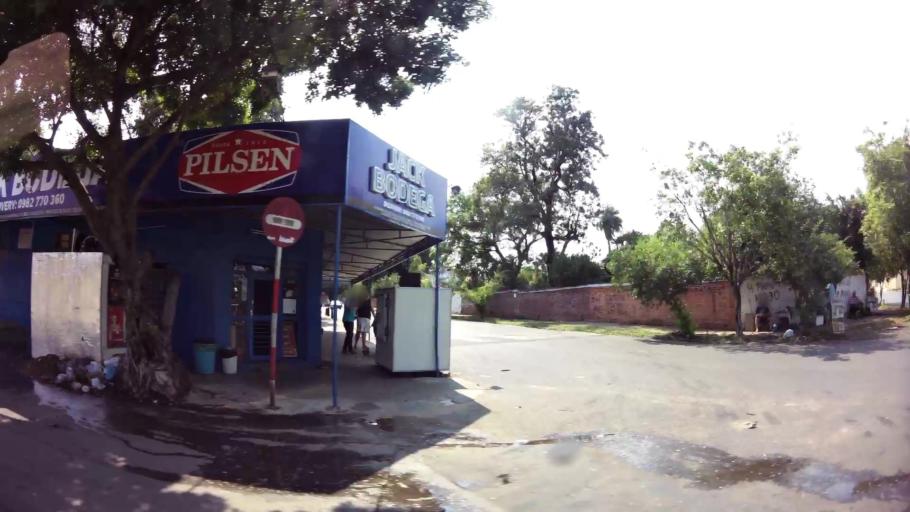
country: PY
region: Asuncion
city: Asuncion
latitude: -25.2945
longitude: -57.6589
